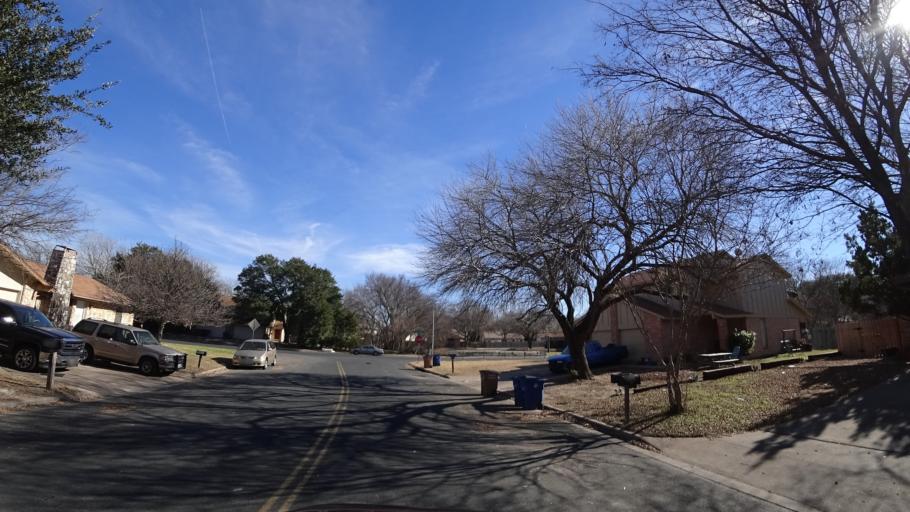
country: US
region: Texas
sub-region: Travis County
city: Wells Branch
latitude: 30.3811
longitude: -97.7111
